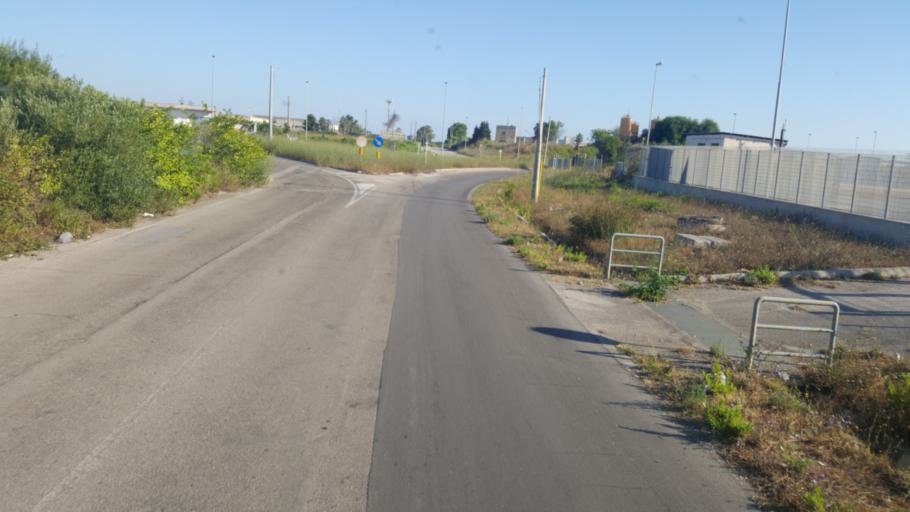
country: IT
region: Apulia
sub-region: Provincia di Brindisi
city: Materdomini
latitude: 40.6341
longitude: 17.9731
